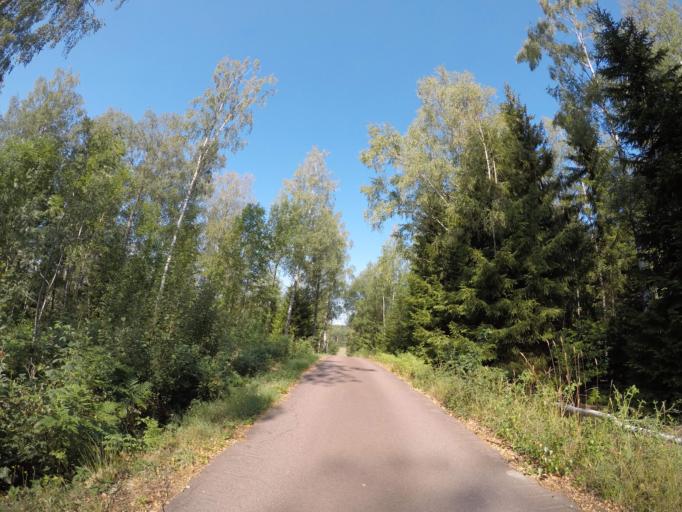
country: AX
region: Alands landsbygd
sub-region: Saltvik
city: Saltvik
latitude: 60.2234
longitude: 20.0126
